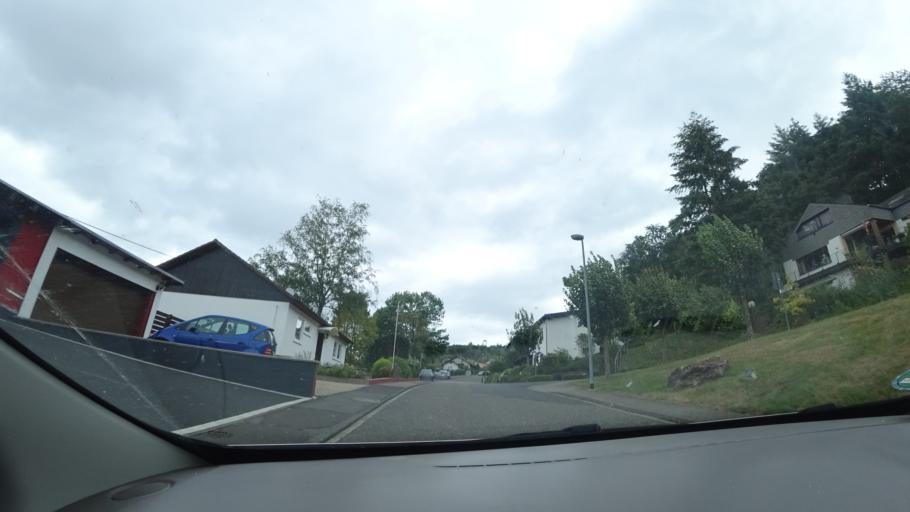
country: DE
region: Rheinland-Pfalz
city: Hillscheid
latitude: 50.4009
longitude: 7.6971
